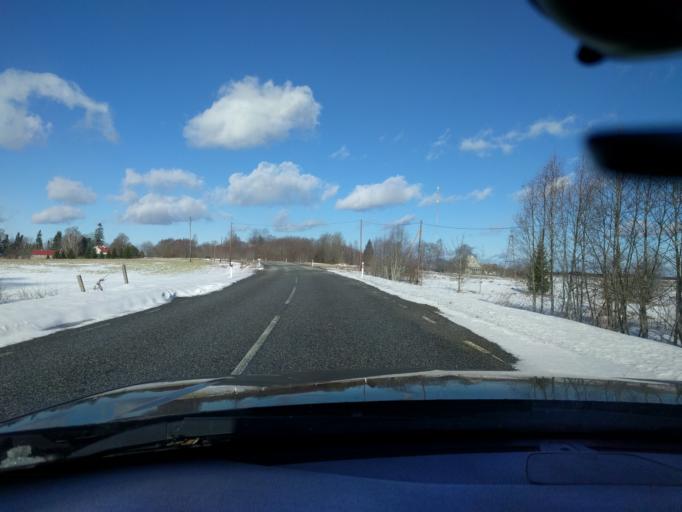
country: EE
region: Harju
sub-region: Raasiku vald
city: Raasiku
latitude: 59.3857
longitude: 25.1956
